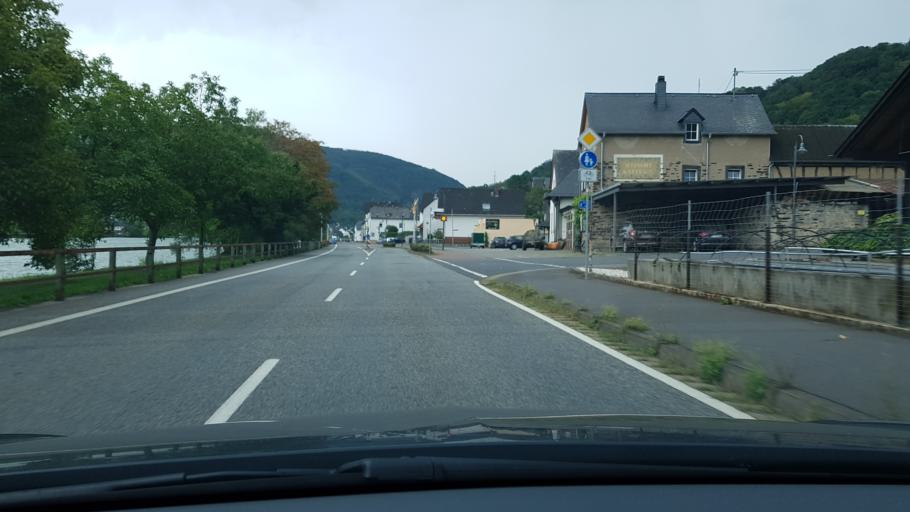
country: DE
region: Rheinland-Pfalz
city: Oberfell
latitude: 50.2546
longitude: 7.4403
